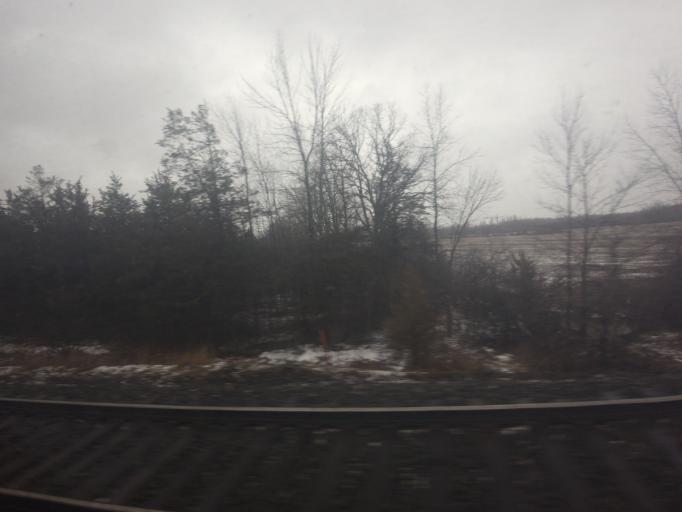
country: CA
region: Ontario
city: Belleville
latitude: 44.2035
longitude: -77.2566
